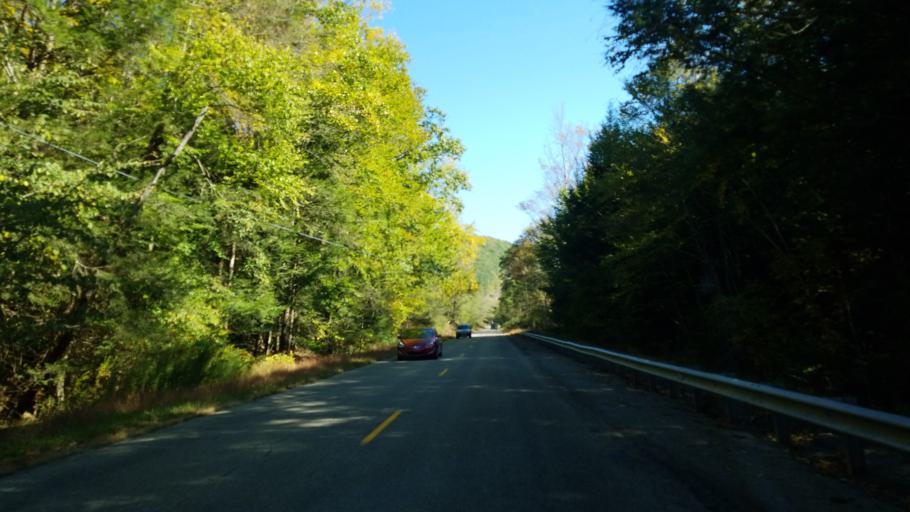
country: US
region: Pennsylvania
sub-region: Elk County
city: Saint Marys
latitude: 41.2650
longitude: -78.3980
